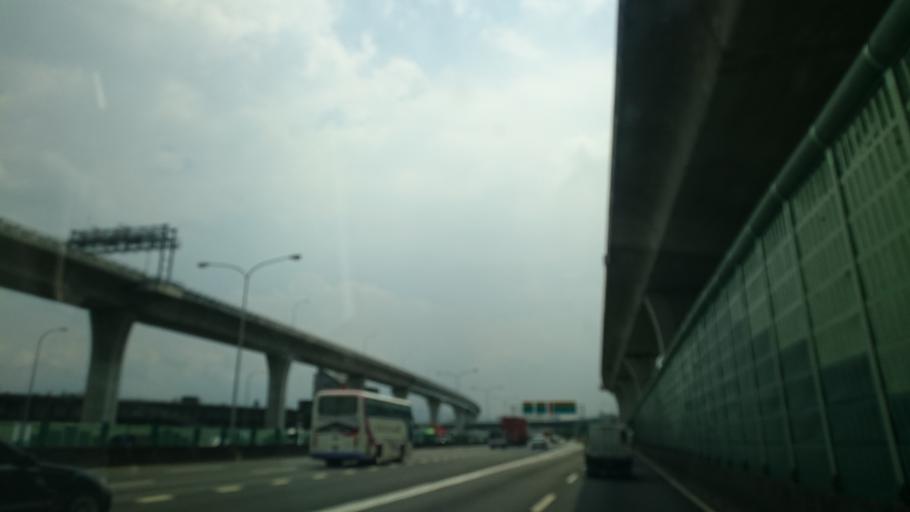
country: TW
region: Taipei
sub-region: Taipei
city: Banqiao
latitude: 25.0681
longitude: 121.4328
